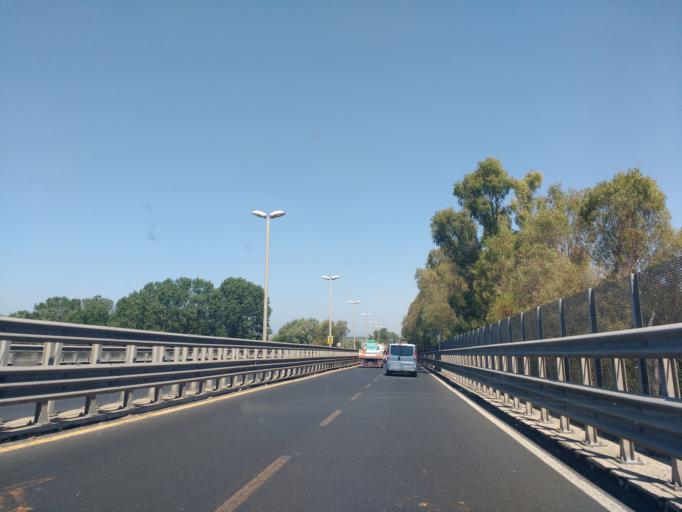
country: IT
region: Latium
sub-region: Citta metropolitana di Roma Capitale
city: Fiumicino-Isola Sacra
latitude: 41.7749
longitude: 12.2540
